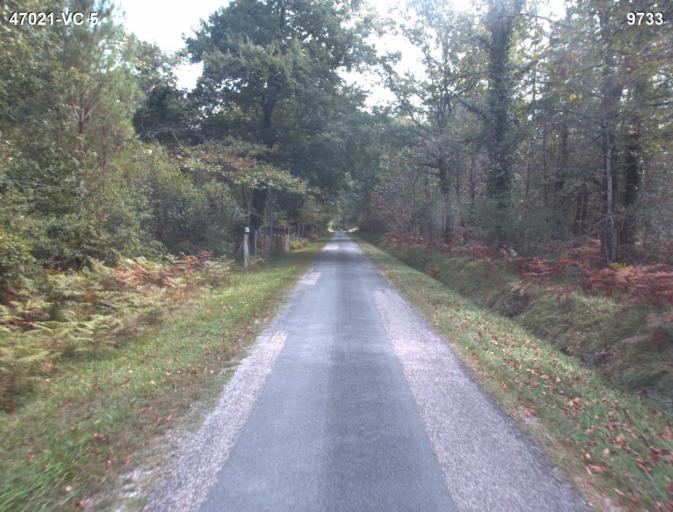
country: FR
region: Aquitaine
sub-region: Departement du Lot-et-Garonne
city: Barbaste
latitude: 44.1597
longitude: 0.1822
